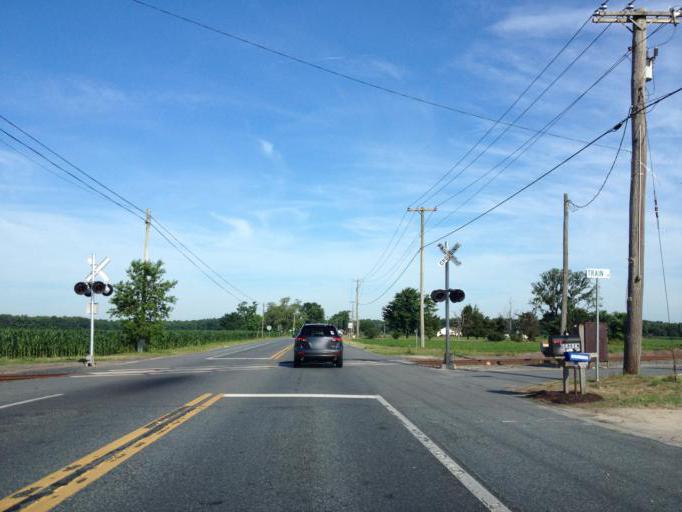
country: US
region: Delaware
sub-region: Sussex County
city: Millsboro
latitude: 38.5547
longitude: -75.2517
